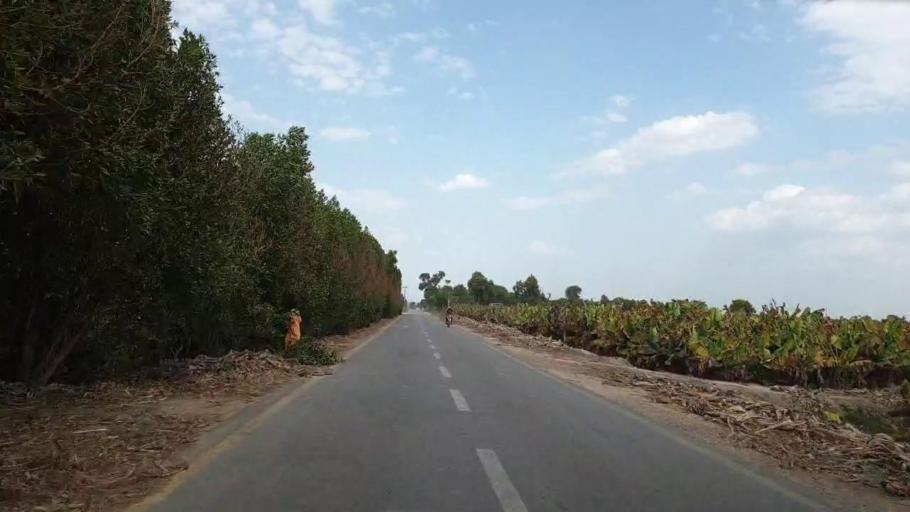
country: PK
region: Sindh
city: Tando Jam
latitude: 25.5055
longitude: 68.6023
